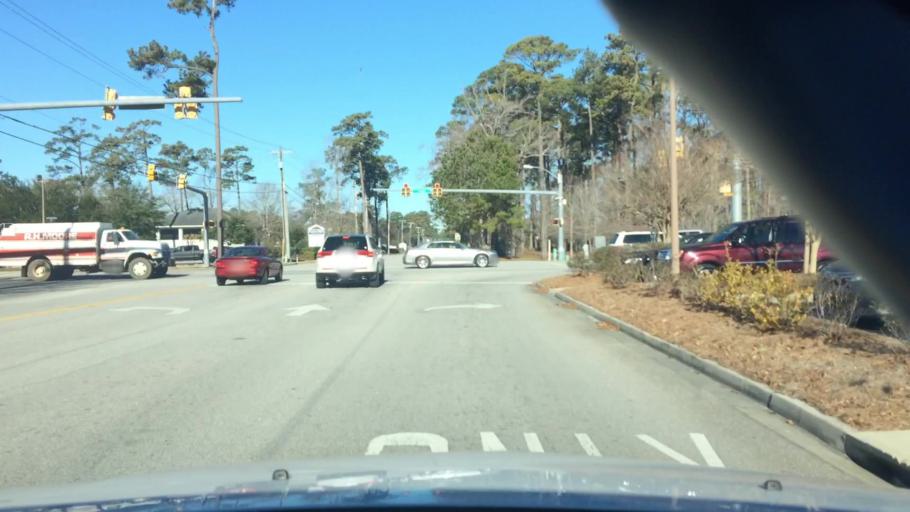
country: US
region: South Carolina
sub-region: Horry County
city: Myrtle Beach
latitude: 33.7303
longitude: -78.8564
